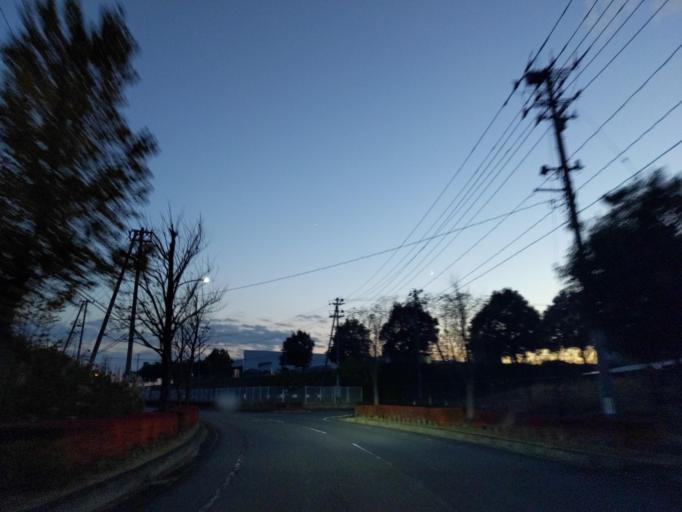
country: JP
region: Fukushima
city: Koriyama
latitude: 37.4496
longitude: 140.3058
